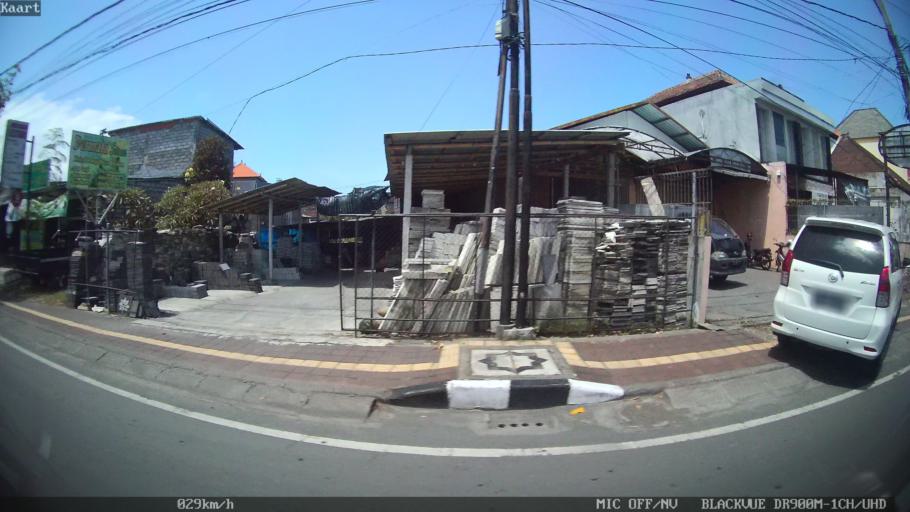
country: ID
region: Bali
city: Denpasar
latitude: -8.6642
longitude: 115.1903
